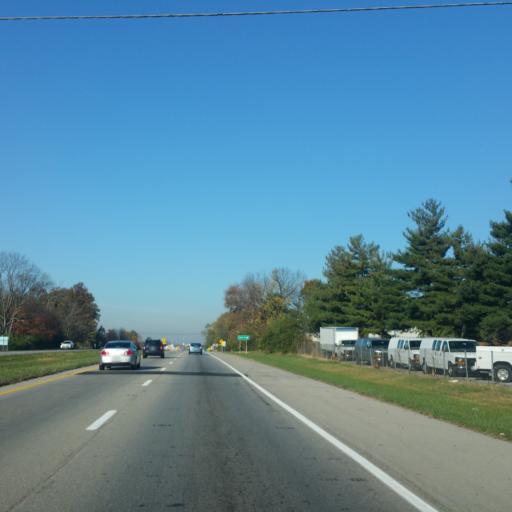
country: US
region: Ohio
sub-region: Clermont County
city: Summerside
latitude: 39.0927
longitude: -84.2547
